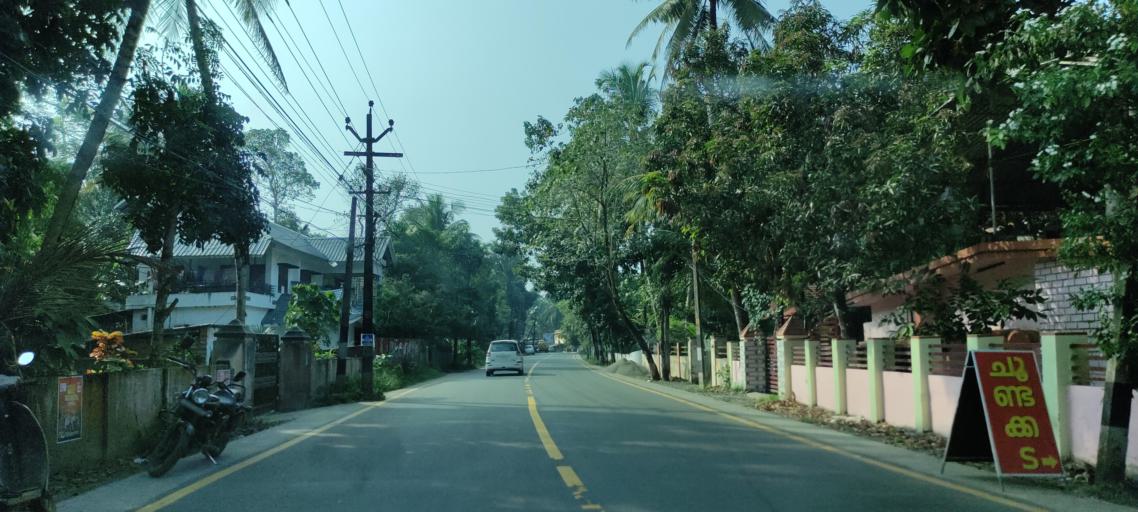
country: IN
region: Kerala
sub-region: Pattanamtitta
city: Tiruvalla
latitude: 9.3705
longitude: 76.5234
